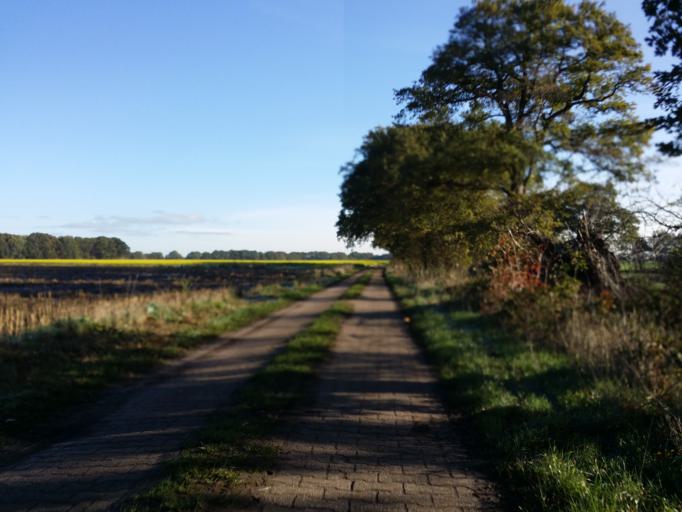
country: DE
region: Lower Saxony
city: Tarmstedt
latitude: 53.2017
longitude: 9.0609
